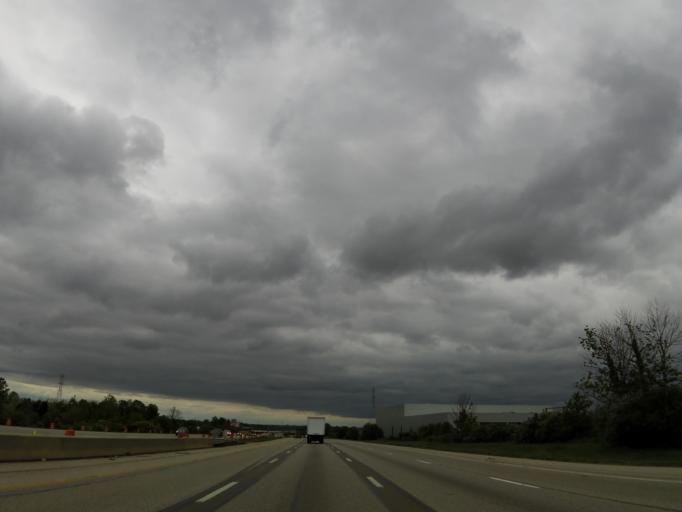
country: US
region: Ohio
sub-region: Warren County
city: Landen
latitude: 39.3228
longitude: -84.2873
